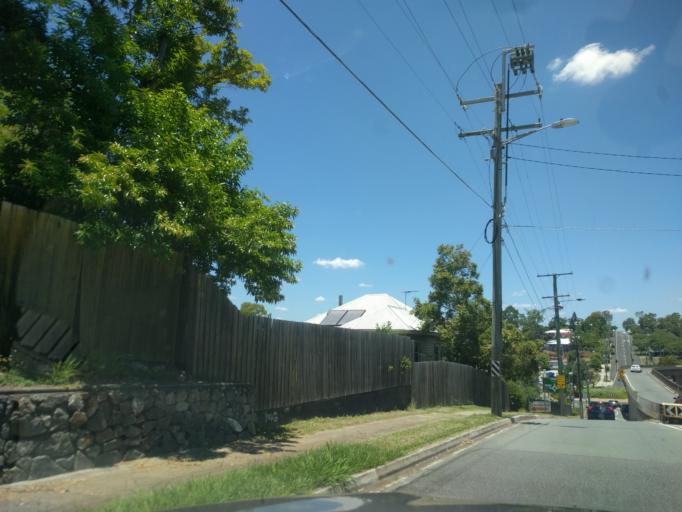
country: AU
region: Queensland
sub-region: Brisbane
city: Toowong
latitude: -27.4770
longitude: 152.9852
